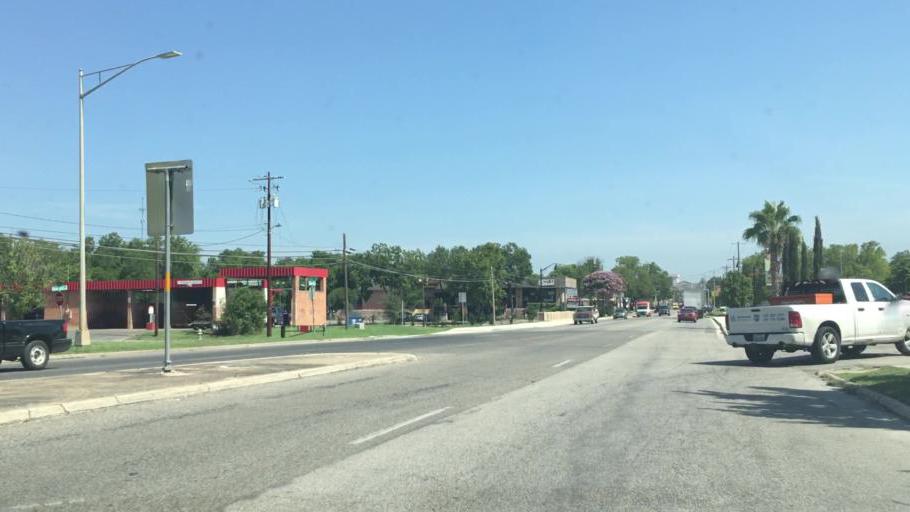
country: US
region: Texas
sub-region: Hays County
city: San Marcos
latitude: 29.8709
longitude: -97.9393
